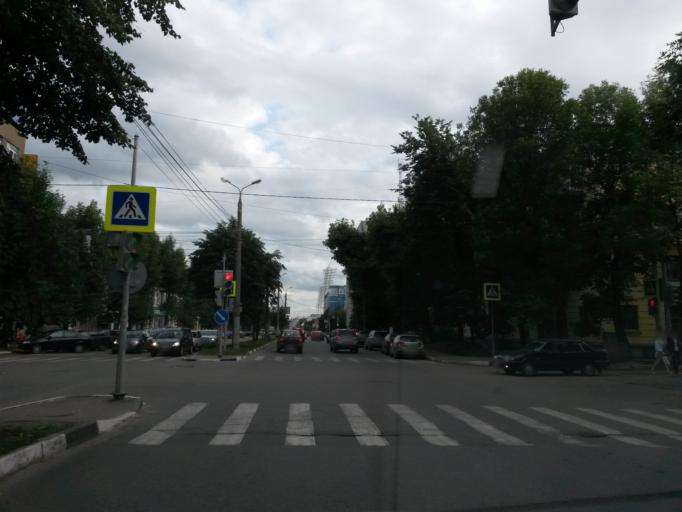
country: RU
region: Jaroslavl
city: Yaroslavl
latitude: 57.6328
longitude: 39.8707
